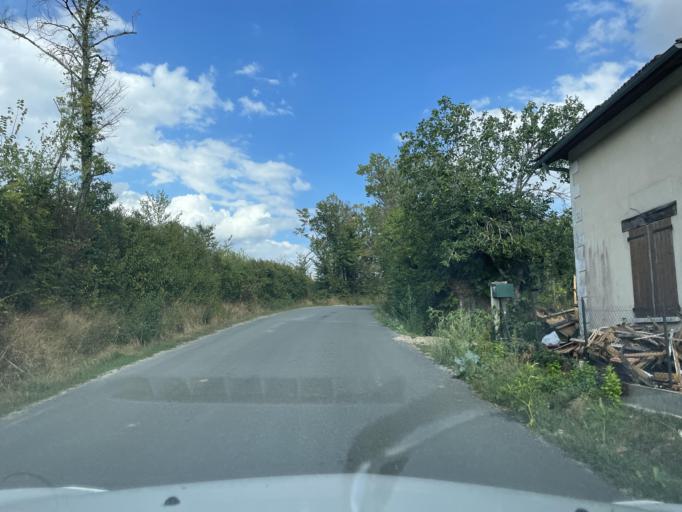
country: FR
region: Aquitaine
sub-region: Departement du Lot-et-Garonne
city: Casteljaloux
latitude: 44.3145
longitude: 0.0944
